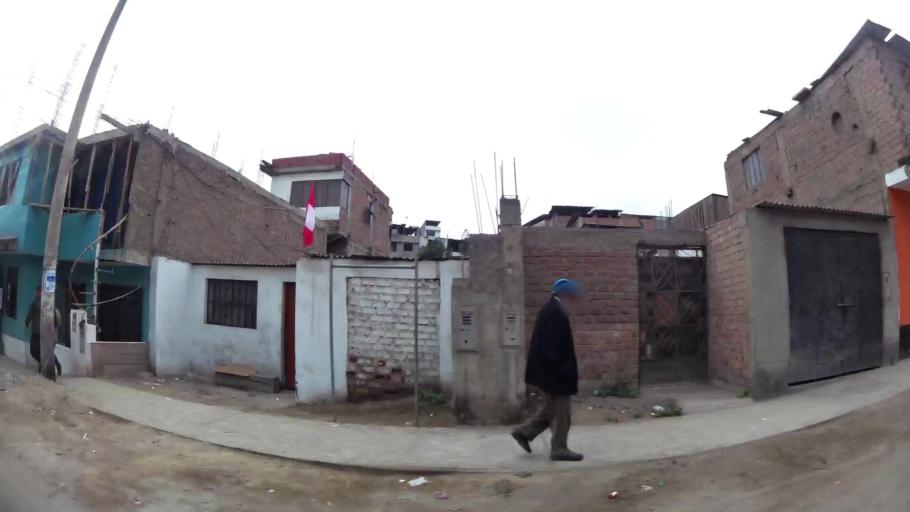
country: PE
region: Lima
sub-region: Lima
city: Surco
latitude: -12.1400
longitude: -76.9606
